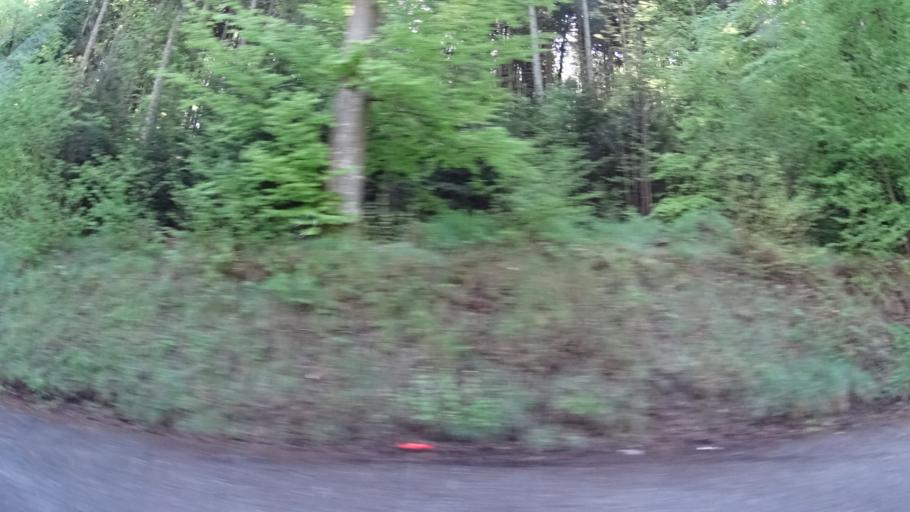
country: DE
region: Baden-Wuerttemberg
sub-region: Karlsruhe Region
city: Bad Wildbad
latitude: 48.7601
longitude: 8.5865
